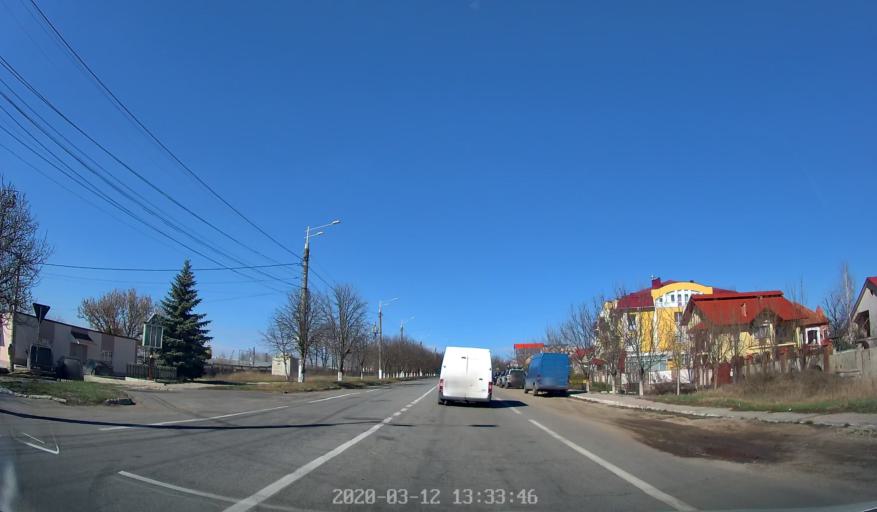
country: MD
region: Laloveni
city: Ialoveni
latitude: 46.9589
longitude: 28.7683
